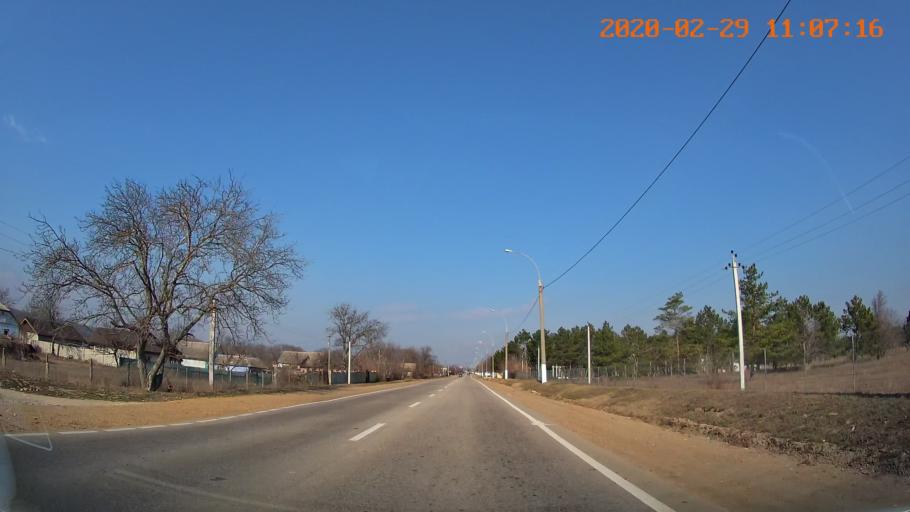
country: MD
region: Criuleni
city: Criuleni
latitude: 47.2237
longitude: 29.1832
